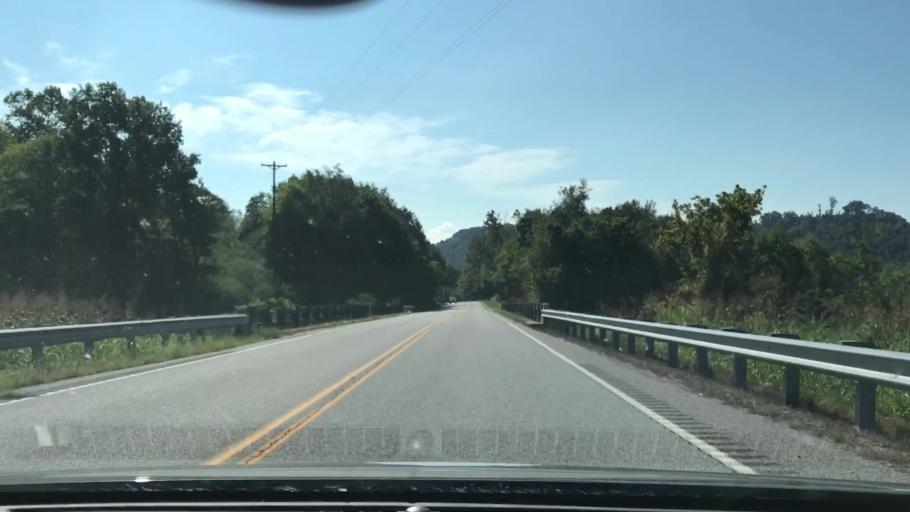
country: US
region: Tennessee
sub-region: Jackson County
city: Gainesboro
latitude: 36.3624
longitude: -85.7535
